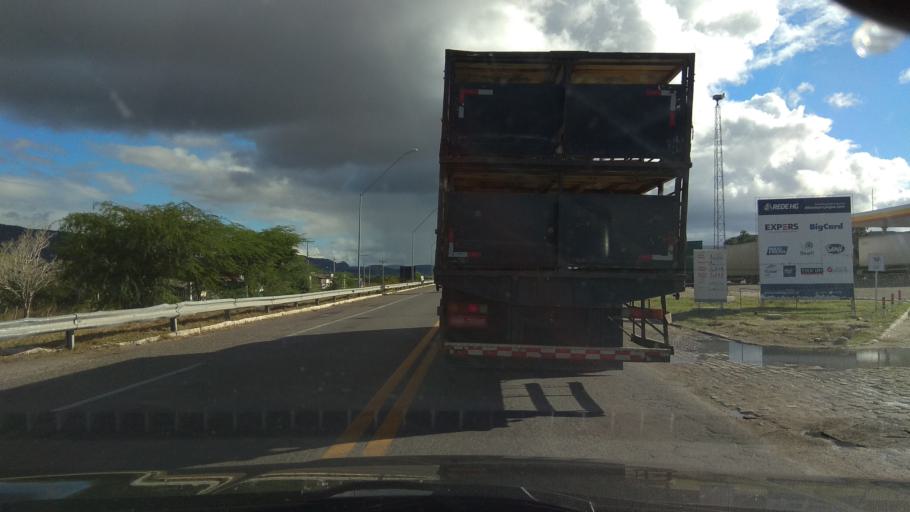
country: BR
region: Bahia
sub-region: Castro Alves
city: Castro Alves
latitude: -12.6972
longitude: -39.7062
